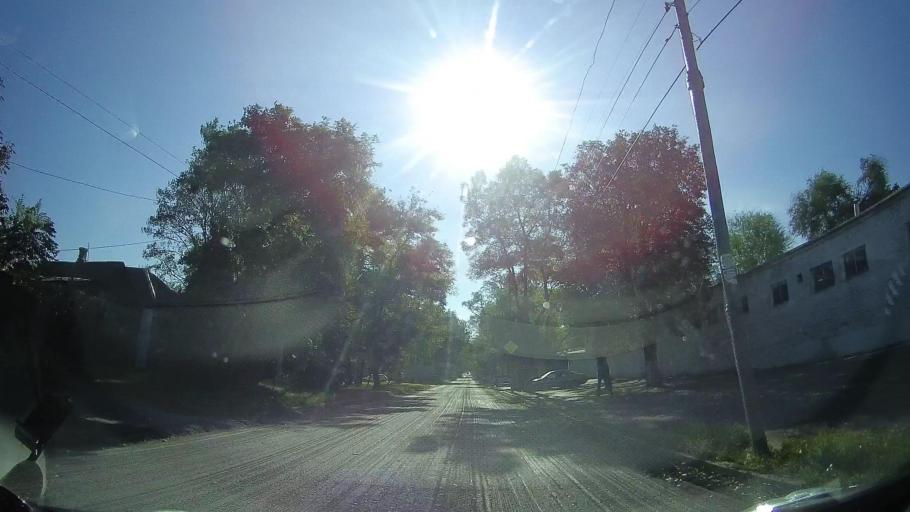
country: RU
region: Rostov
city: Rostov-na-Donu
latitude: 47.2381
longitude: 39.7291
